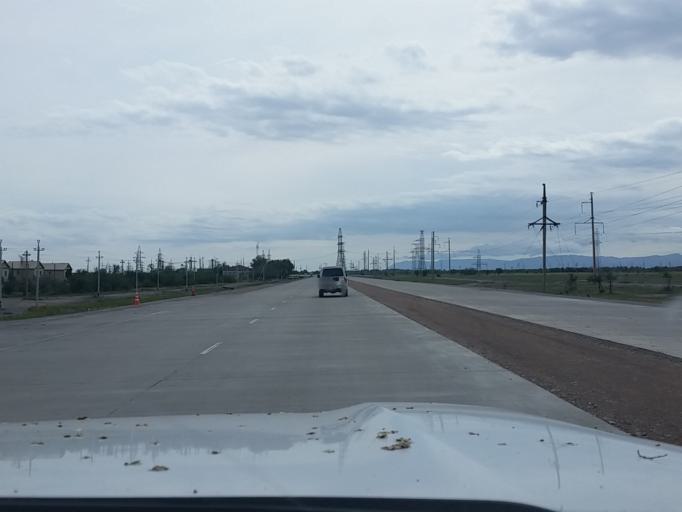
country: KZ
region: Almaty Oblysy
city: Turgen'
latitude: 43.5829
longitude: 78.2565
